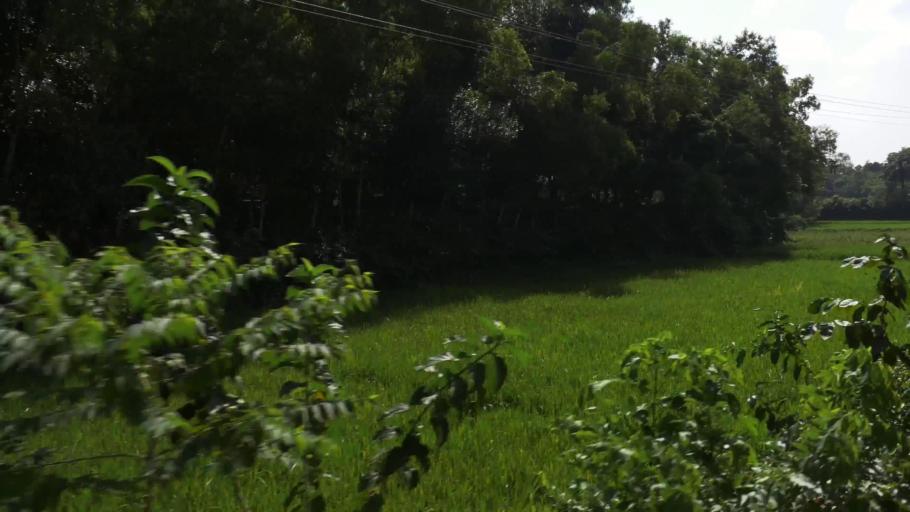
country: BD
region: Dhaka
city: Gafargaon
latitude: 24.2541
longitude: 90.4961
